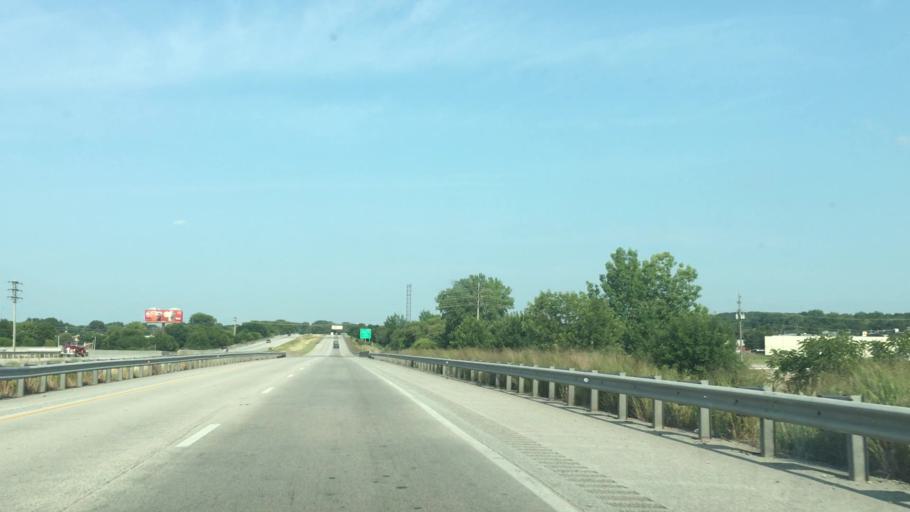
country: US
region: Illinois
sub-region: Rock Island County
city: Milan
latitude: 41.4461
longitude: -90.5741
